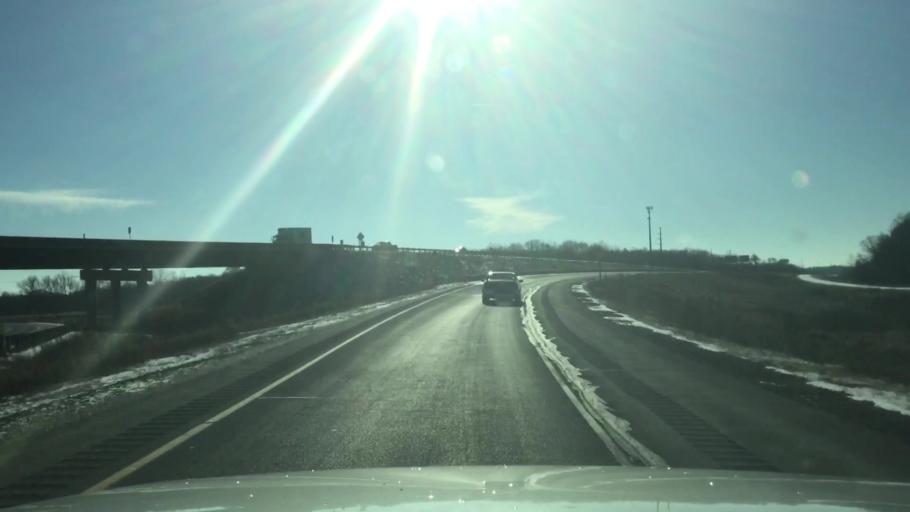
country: US
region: Wisconsin
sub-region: Racine County
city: Rochester
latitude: 42.7175
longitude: -88.2260
